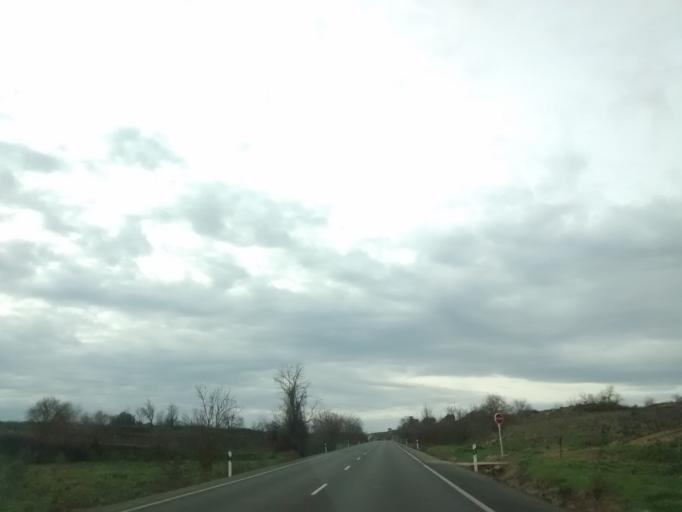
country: ES
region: La Rioja
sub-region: Provincia de La Rioja
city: Torremontalbo
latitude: 42.5096
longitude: -2.7140
